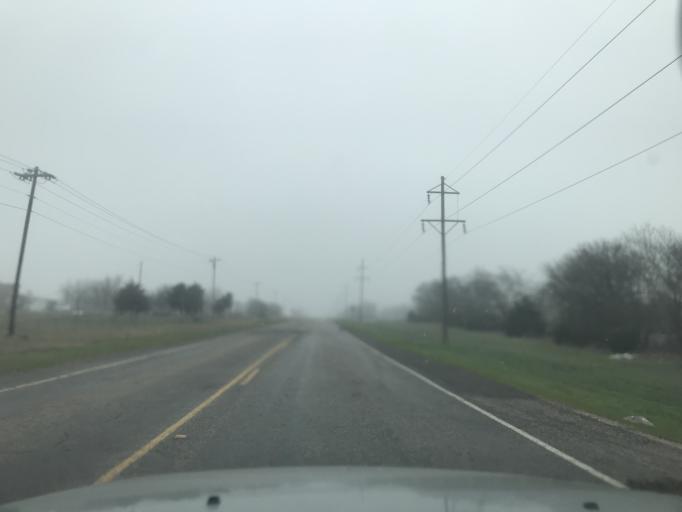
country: US
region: Texas
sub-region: Hunt County
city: Caddo Mills
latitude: 33.0231
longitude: -96.2757
